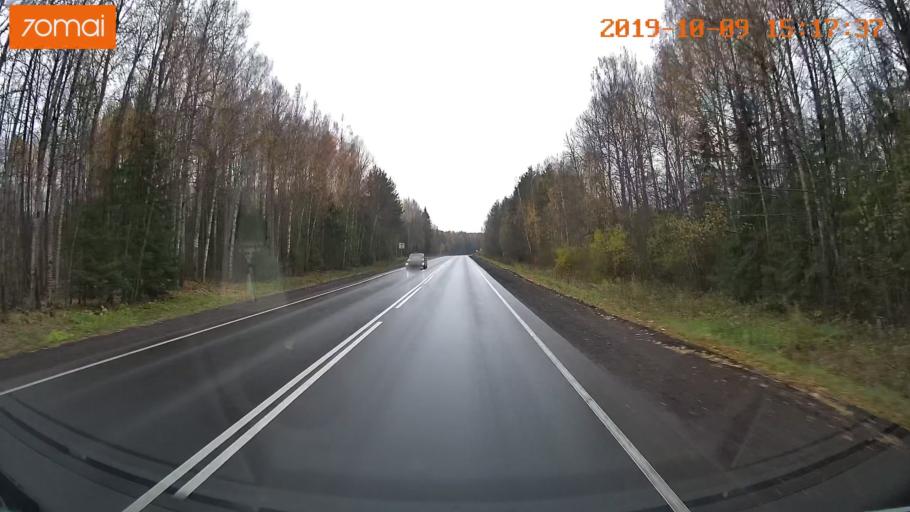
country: RU
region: Kostroma
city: Susanino
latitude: 58.0960
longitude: 41.5821
